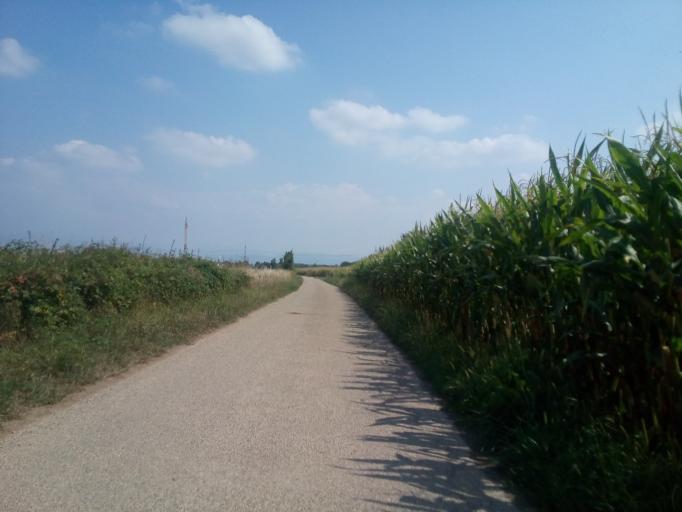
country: DE
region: Baden-Wuerttemberg
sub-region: Freiburg Region
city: Rheinau
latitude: 48.6344
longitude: 7.9099
